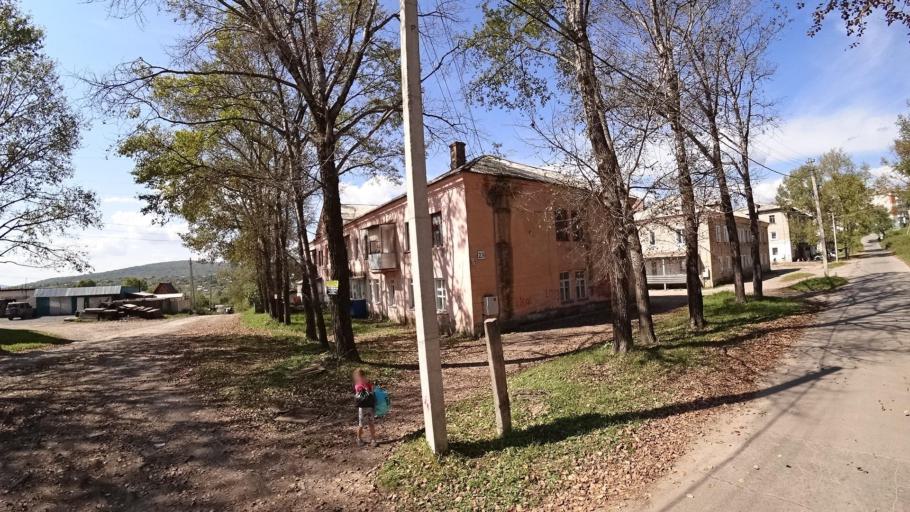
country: RU
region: Jewish Autonomous Oblast
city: Londoko
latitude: 49.0112
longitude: 131.8829
